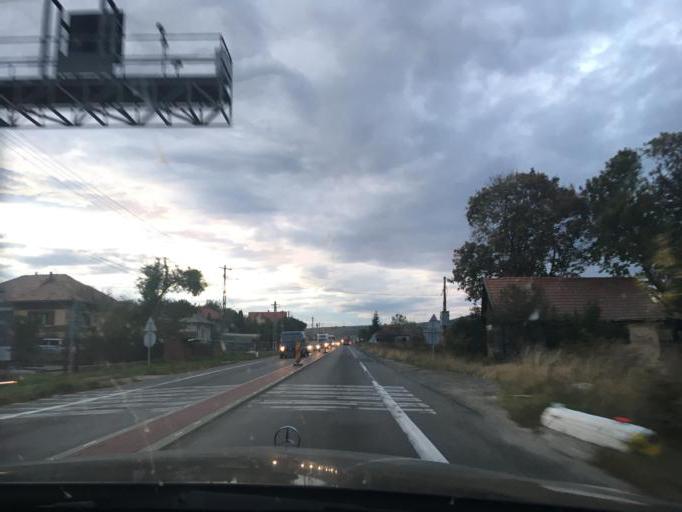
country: RO
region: Cluj
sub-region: Comuna Aghiresu
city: Aghiresu
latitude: 46.8146
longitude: 23.1809
